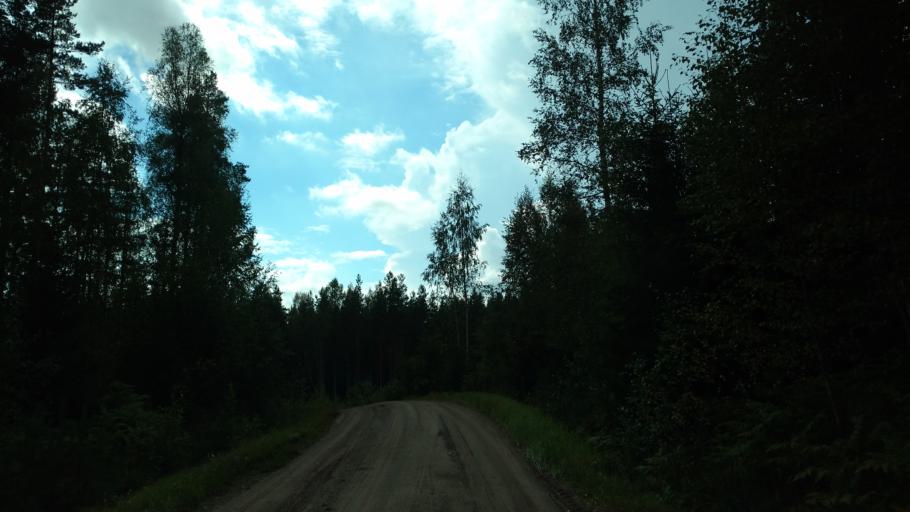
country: FI
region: Varsinais-Suomi
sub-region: Salo
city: Kiikala
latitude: 60.4889
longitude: 23.6326
